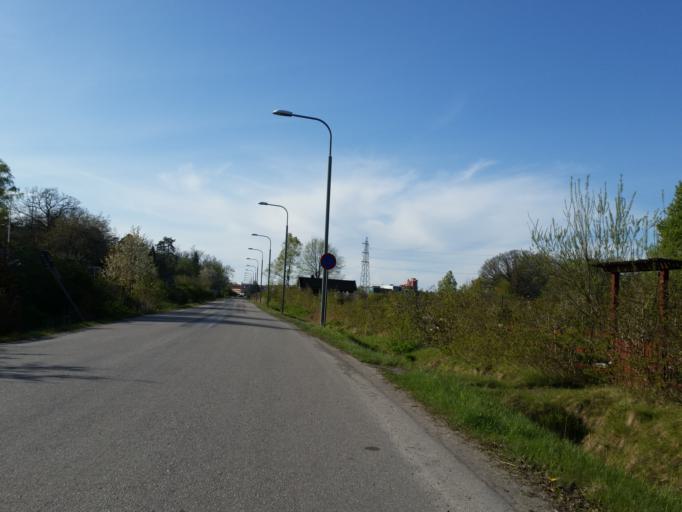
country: SE
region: Stockholm
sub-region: Nacka Kommun
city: Alta
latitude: 59.2583
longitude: 18.1359
